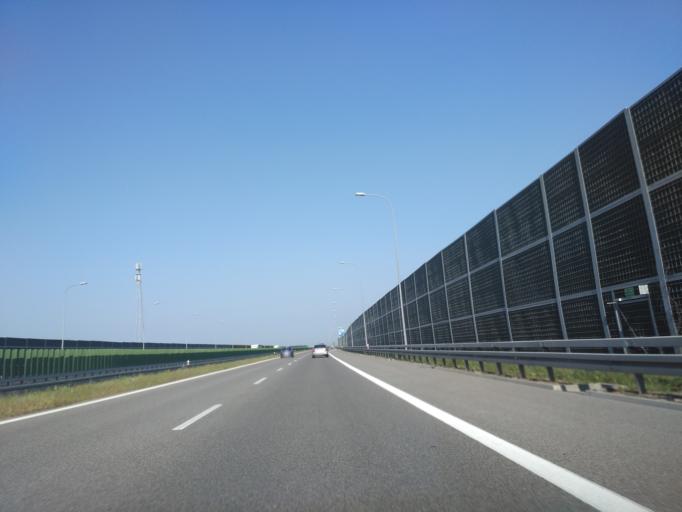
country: PL
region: Subcarpathian Voivodeship
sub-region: Powiat rzeszowski
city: Trzciana
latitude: 50.1084
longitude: 21.8551
